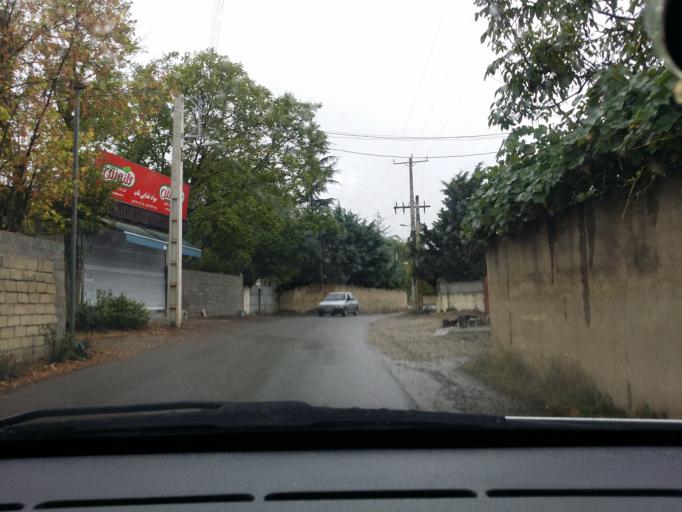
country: IR
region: Mazandaran
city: Chalus
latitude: 36.5285
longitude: 51.2265
